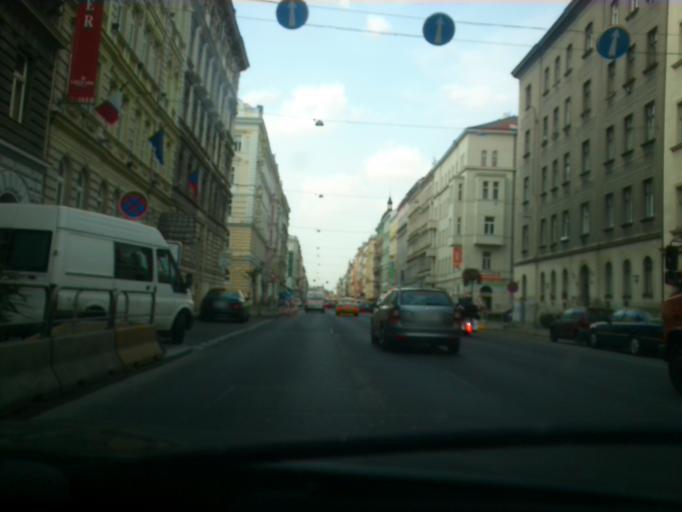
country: CZ
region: Praha
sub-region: Praha 2
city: Vysehrad
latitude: 50.0701
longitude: 14.4308
